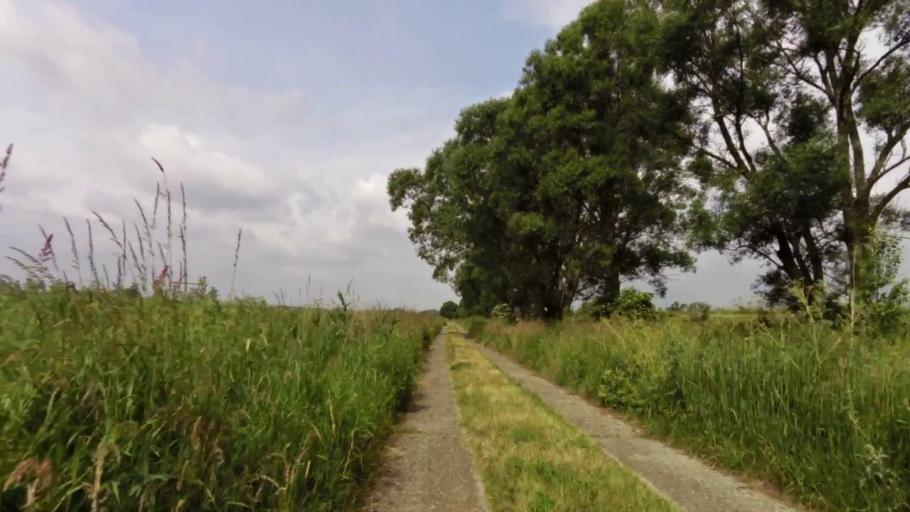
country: PL
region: West Pomeranian Voivodeship
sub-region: Powiat goleniowski
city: Stepnica
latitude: 53.5525
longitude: 14.6999
